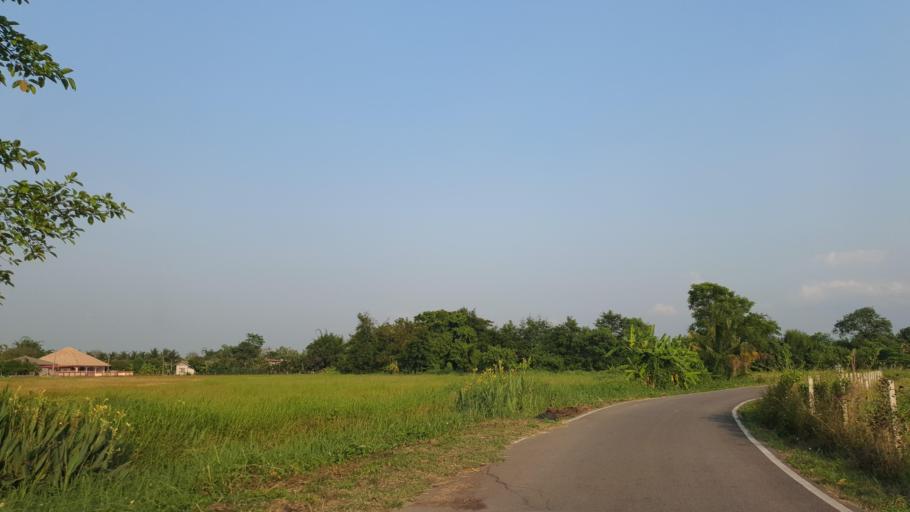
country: TH
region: Chiang Mai
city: San Pa Tong
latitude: 18.6394
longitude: 98.8747
